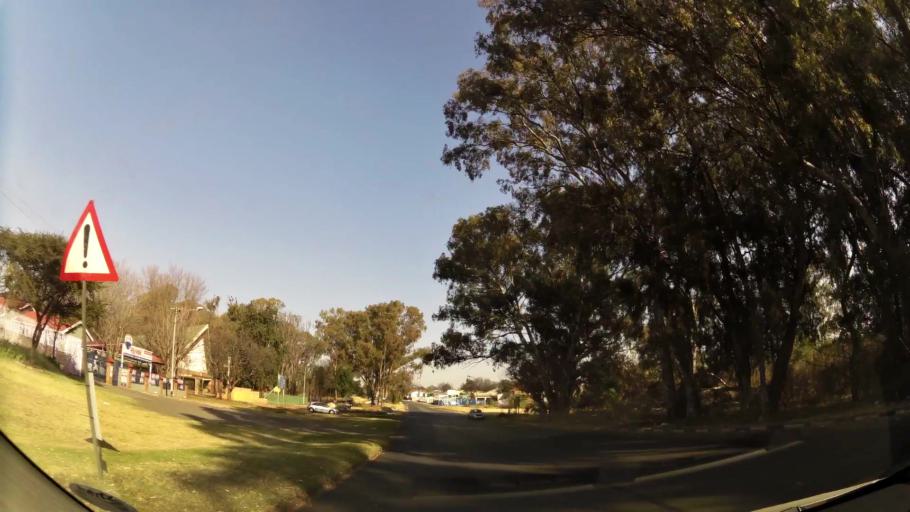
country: ZA
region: Gauteng
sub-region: West Rand District Municipality
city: Randfontein
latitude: -26.1669
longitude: 27.6893
